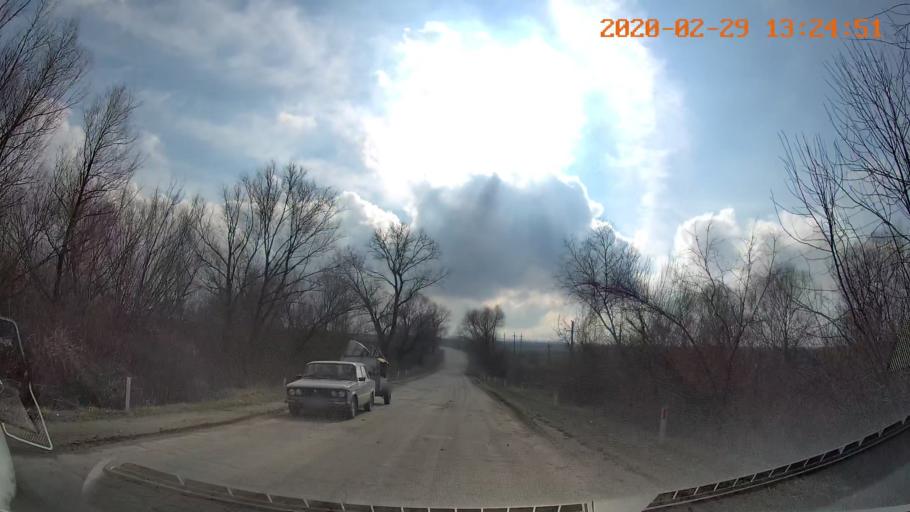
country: MD
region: Telenesti
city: Camenca
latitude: 47.9348
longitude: 28.6284
